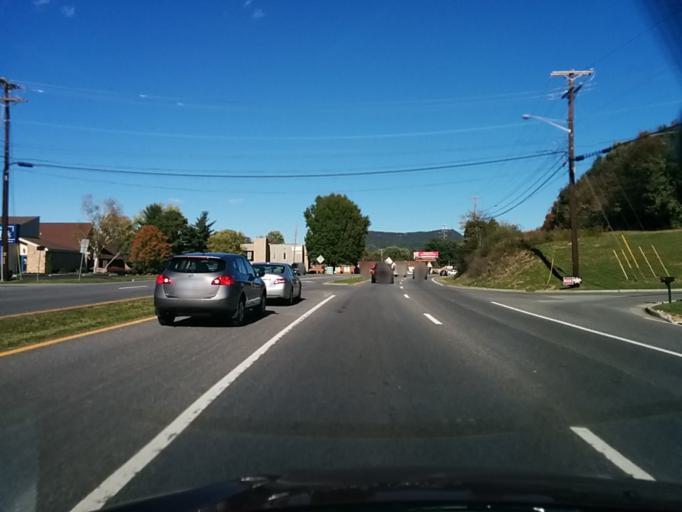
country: US
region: Virginia
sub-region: Roanoke County
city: Hollins
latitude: 37.3417
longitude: -79.9691
